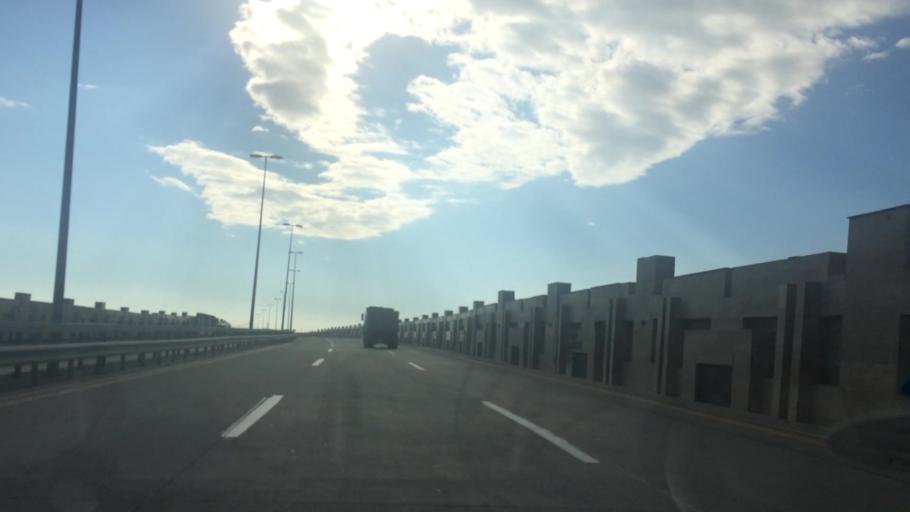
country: AZ
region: Baki
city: Hovsan
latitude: 40.3920
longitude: 50.0742
